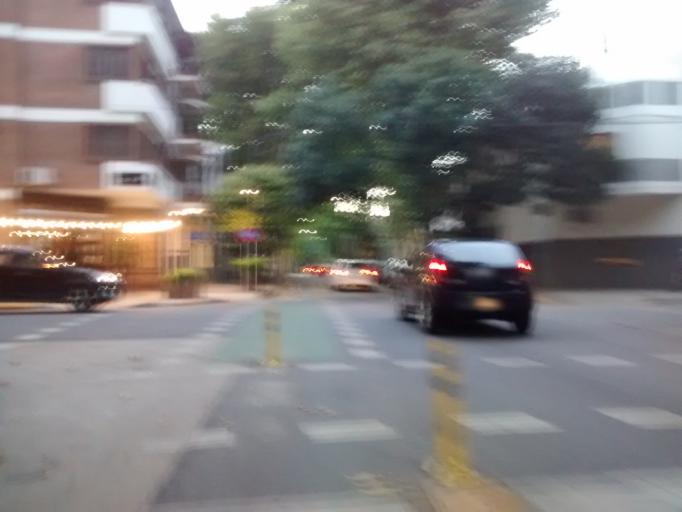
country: AR
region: Buenos Aires F.D.
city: Villa Santa Rita
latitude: -34.6058
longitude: -58.4543
